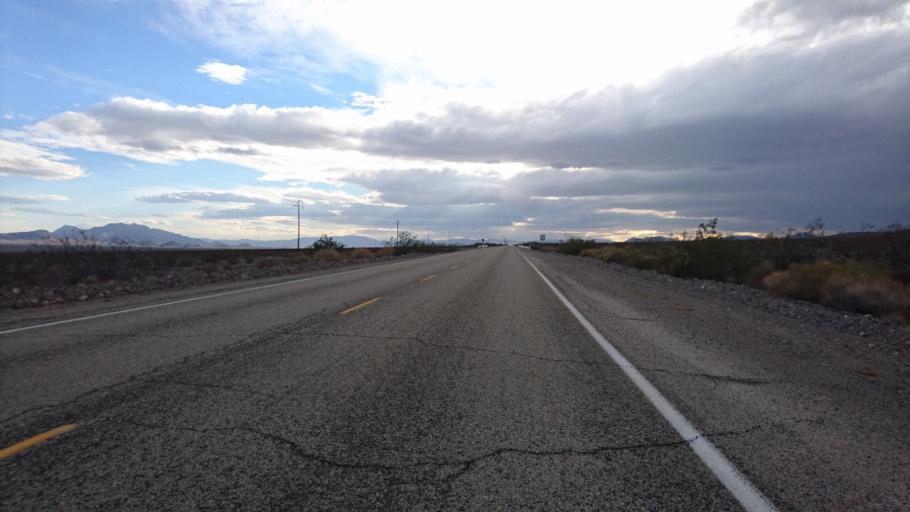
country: US
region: California
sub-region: San Bernardino County
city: Needles
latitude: 34.6652
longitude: -115.3476
